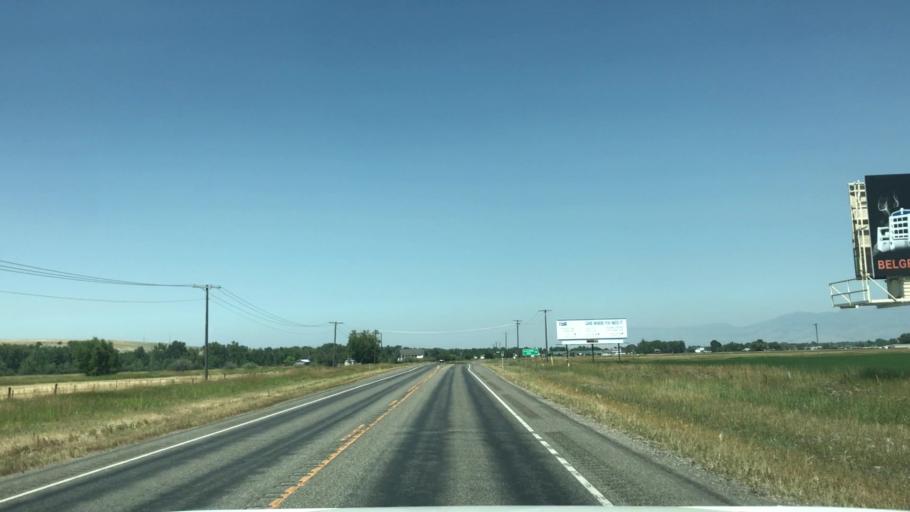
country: US
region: Montana
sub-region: Gallatin County
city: Four Corners
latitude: 45.6362
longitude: -111.1968
